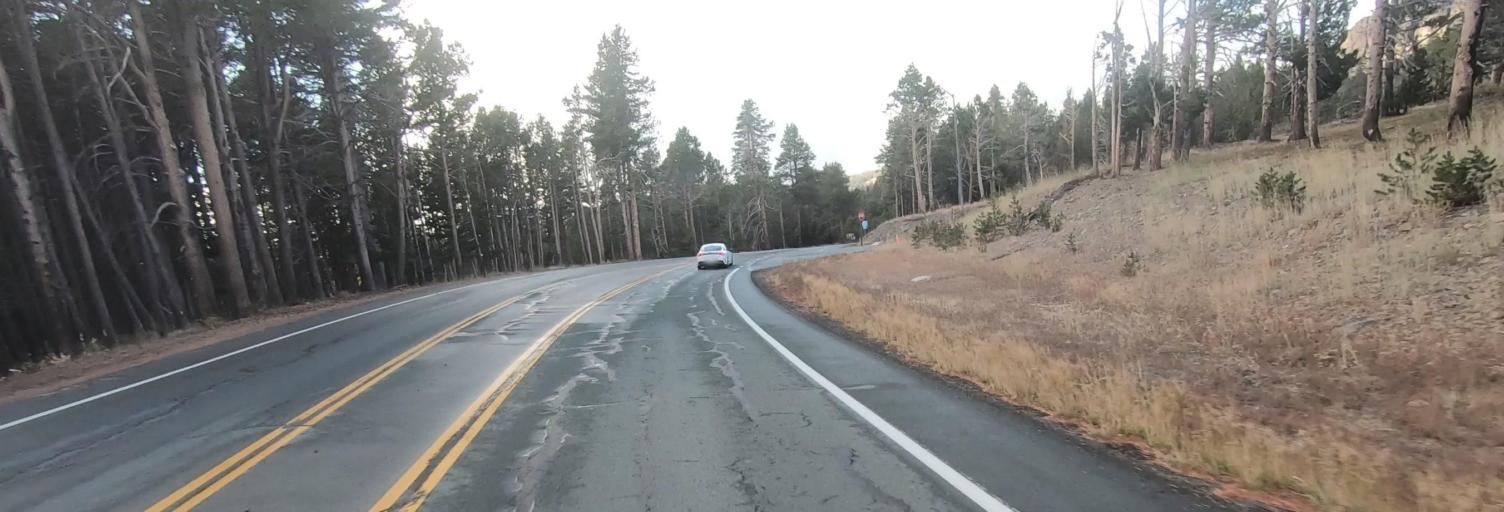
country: US
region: California
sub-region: El Dorado County
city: South Lake Tahoe
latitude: 38.7038
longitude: -120.0379
